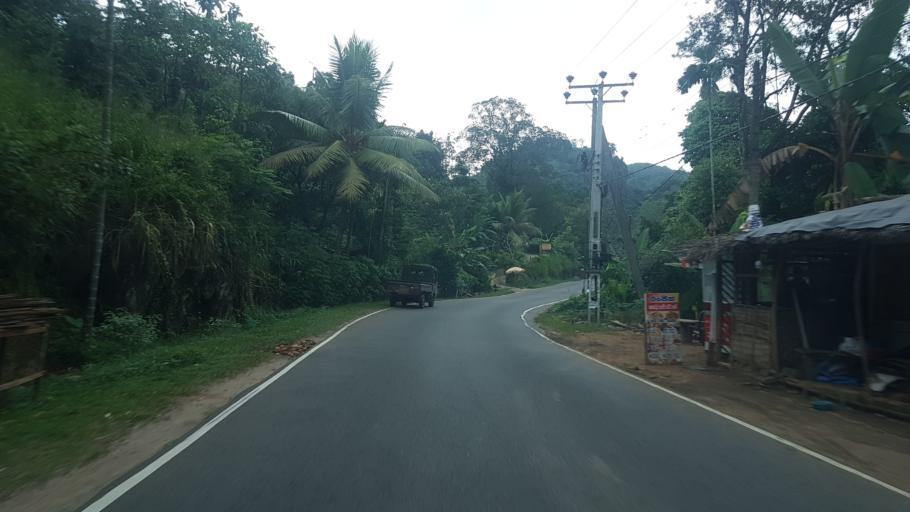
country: LK
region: Western
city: Hanwella Ihala
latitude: 7.0312
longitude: 80.2839
